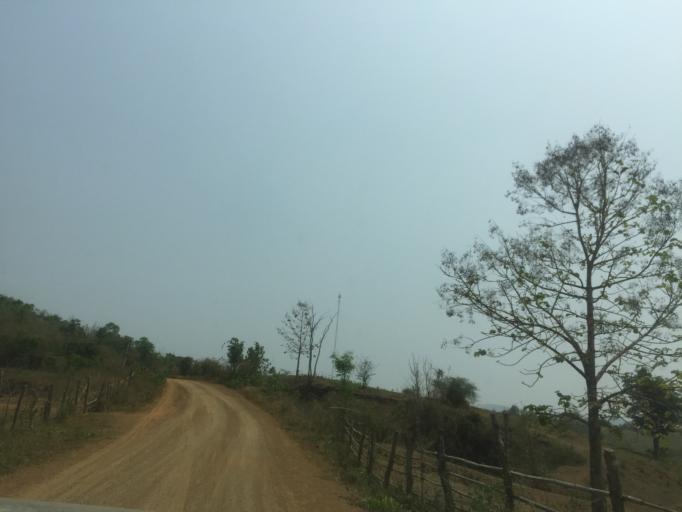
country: LA
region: Xiagnabouli
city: Muang Kenthao
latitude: 17.7956
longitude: 101.2597
